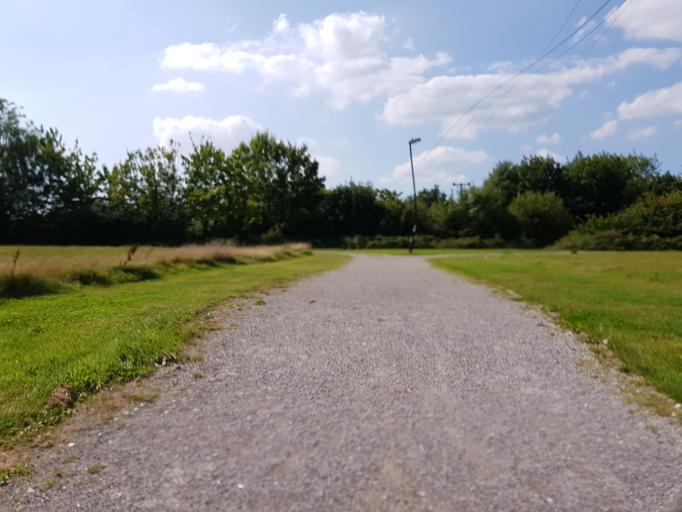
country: GB
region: England
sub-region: Hampshire
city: Waterlooville
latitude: 50.8767
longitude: -1.0410
